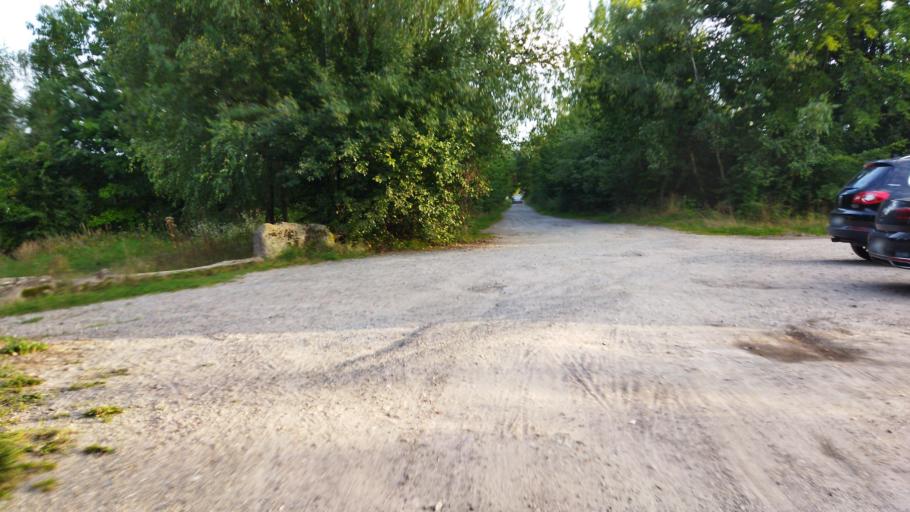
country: DE
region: Lower Saxony
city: Glandorf
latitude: 52.0975
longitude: 8.0362
